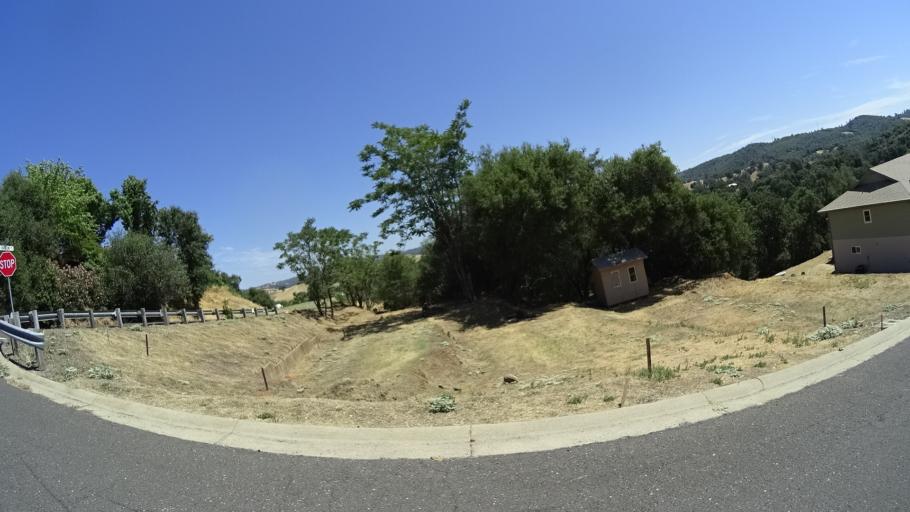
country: US
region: California
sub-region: Calaveras County
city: Angels Camp
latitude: 38.0673
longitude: -120.5422
